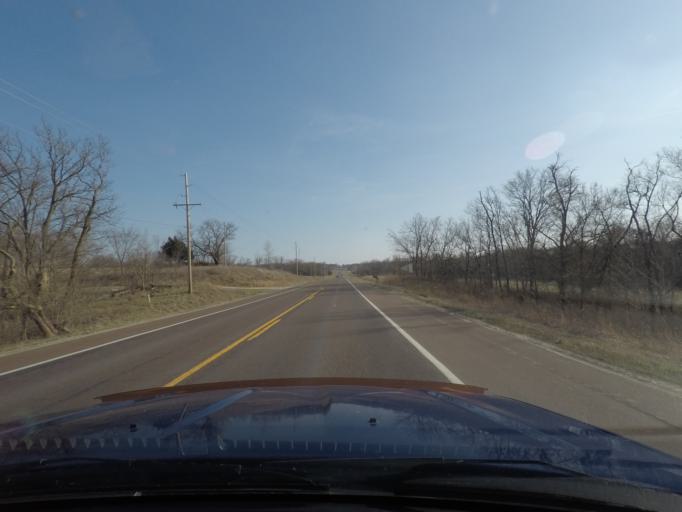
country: US
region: Kansas
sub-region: Douglas County
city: Lawrence
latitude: 39.0135
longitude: -95.3914
